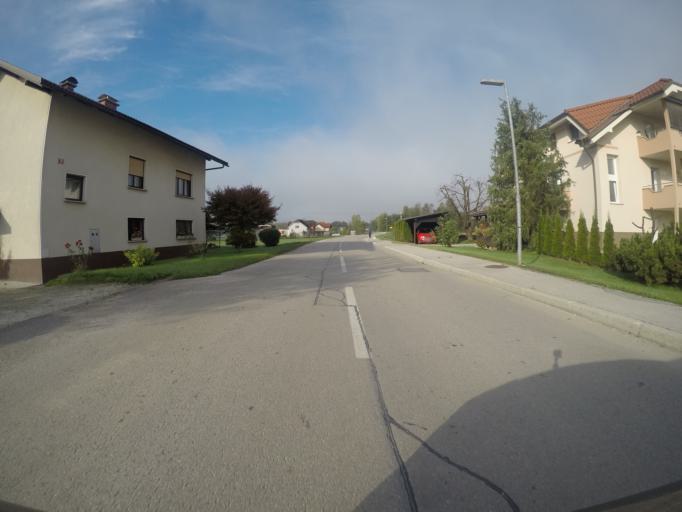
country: SI
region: Domzale
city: Dob
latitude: 46.1495
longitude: 14.6443
